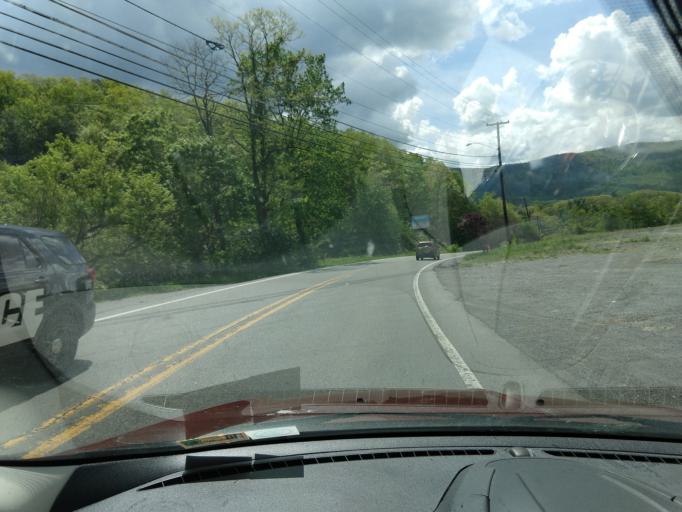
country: US
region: West Virginia
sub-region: Mercer County
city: Bluefield
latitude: 37.2600
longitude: -81.2347
